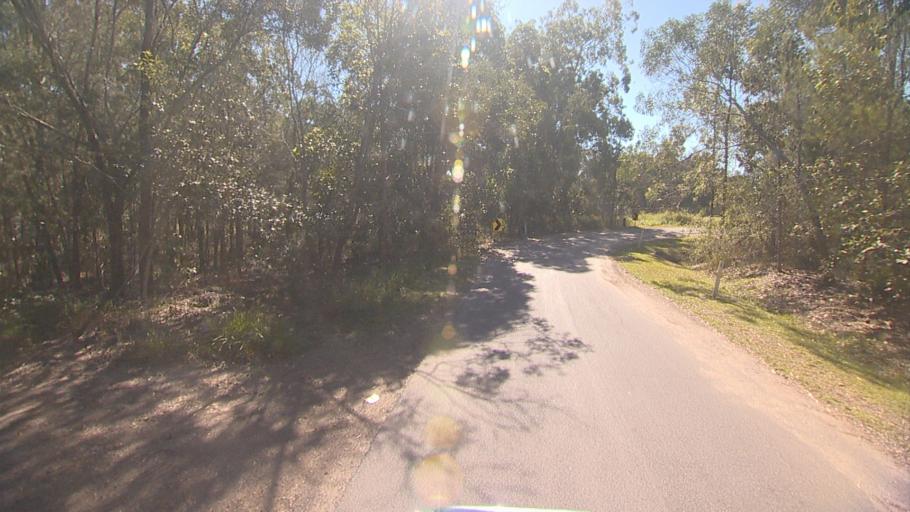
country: AU
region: Queensland
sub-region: Logan
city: Park Ridge South
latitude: -27.6876
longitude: 153.0060
